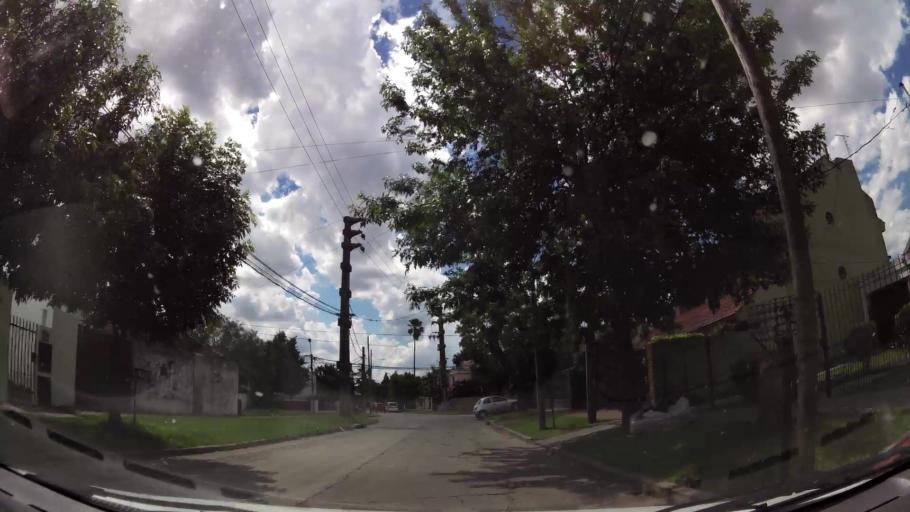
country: AR
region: Buenos Aires
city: Ituzaingo
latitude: -34.6480
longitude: -58.6747
